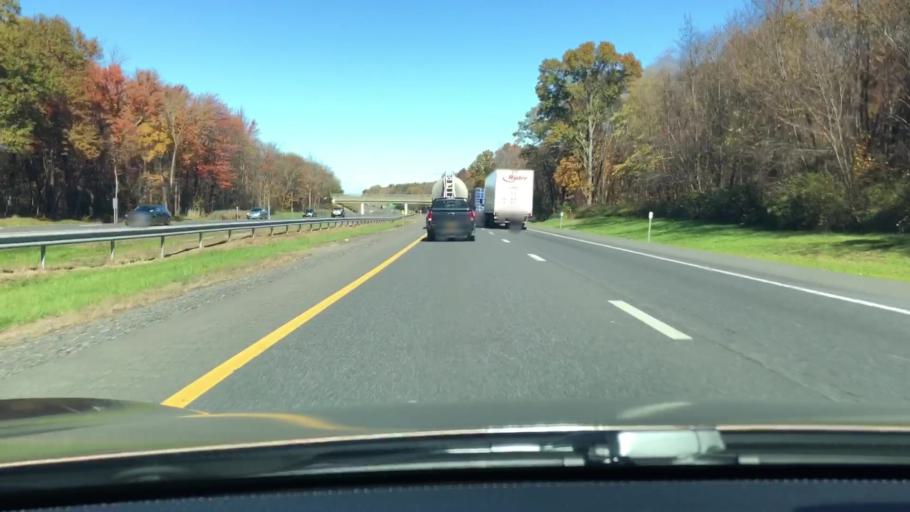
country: US
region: New York
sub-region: Ulster County
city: Clintondale
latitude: 41.7076
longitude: -74.0760
